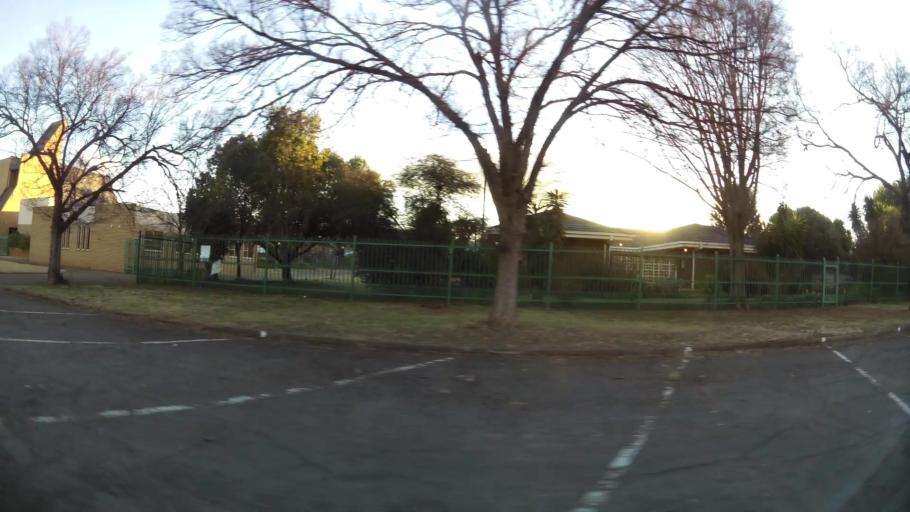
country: ZA
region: North-West
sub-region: Dr Kenneth Kaunda District Municipality
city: Potchefstroom
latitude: -26.7217
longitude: 27.0857
